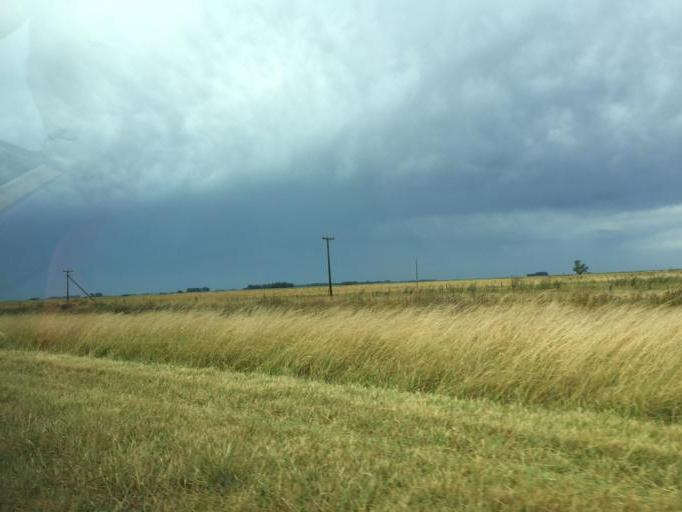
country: AR
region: Buenos Aires
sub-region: Partido de Rauch
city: Rauch
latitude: -36.9565
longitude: -58.9924
